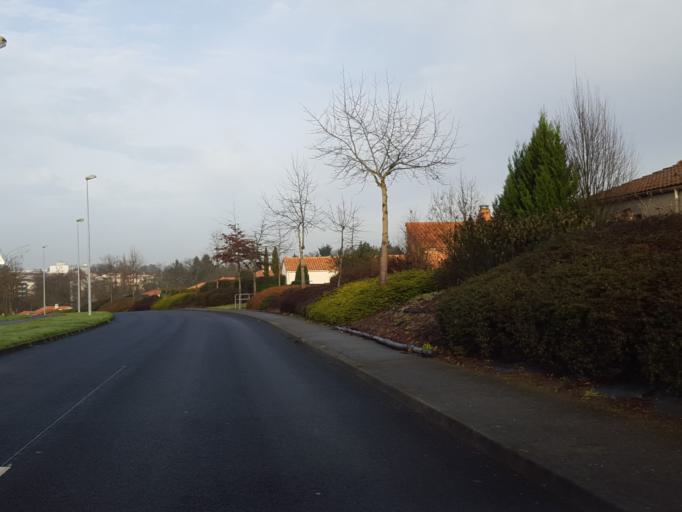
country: FR
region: Pays de la Loire
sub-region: Departement de la Vendee
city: La Roche-sur-Yon
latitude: 46.6793
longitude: -1.4095
